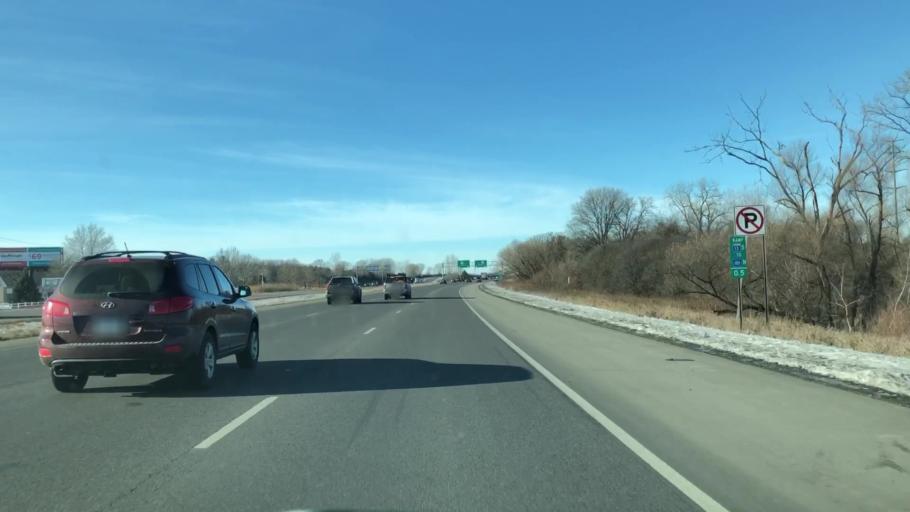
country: US
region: Minnesota
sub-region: Scott County
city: Savage
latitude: 44.7813
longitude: -93.3872
